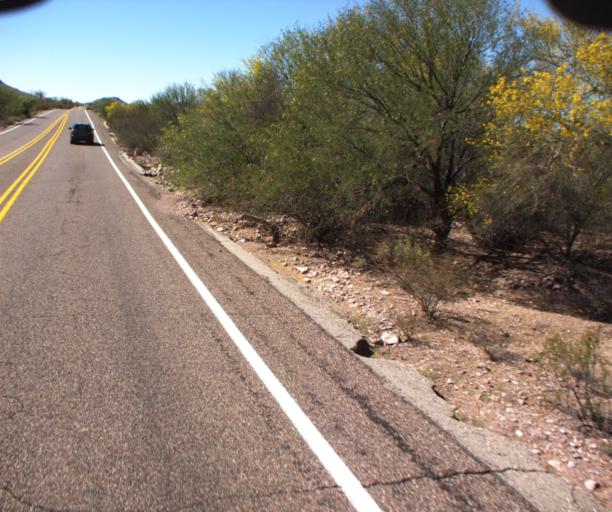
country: US
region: Arizona
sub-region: Pima County
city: Ajo
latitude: 32.1278
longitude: -112.7680
